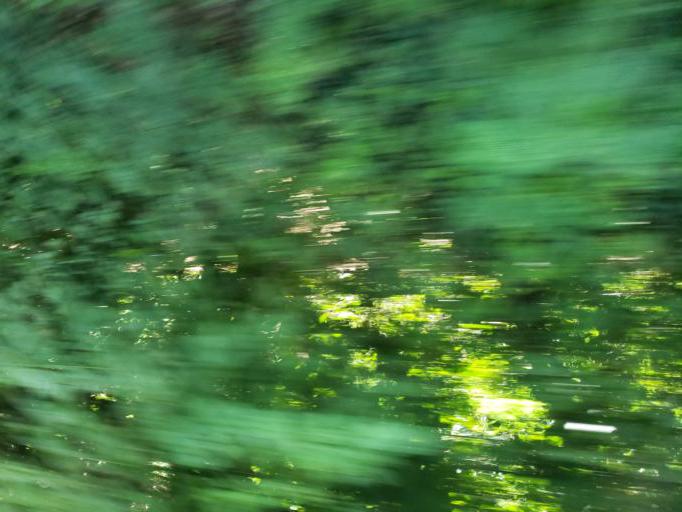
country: ID
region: Bali
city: Kangin
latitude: -8.8212
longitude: 115.1527
